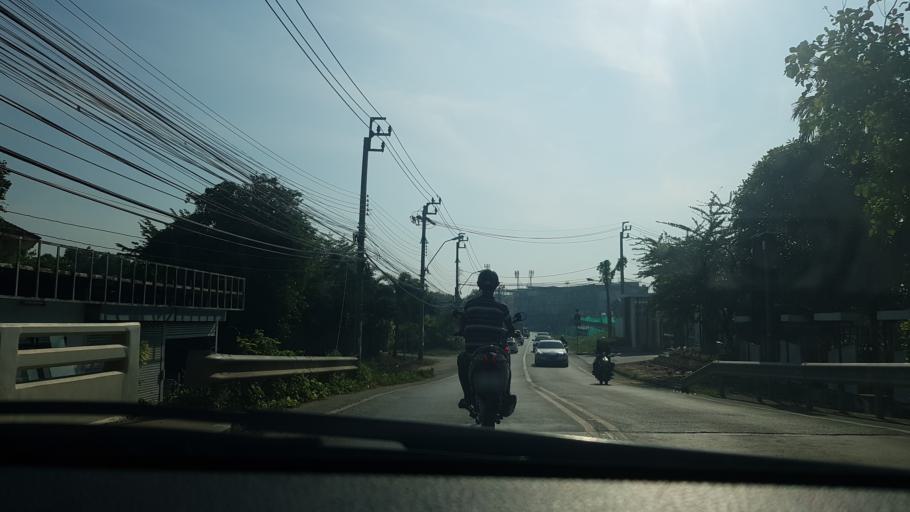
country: TH
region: Bangkok
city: Thawi Watthana
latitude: 13.7987
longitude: 100.3692
